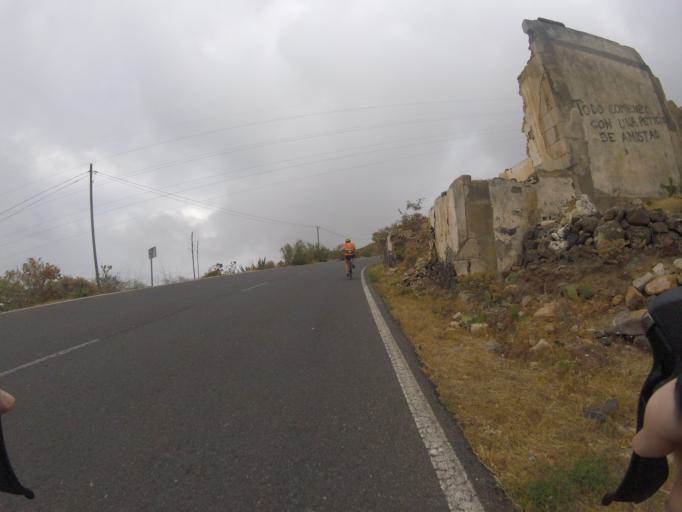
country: ES
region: Canary Islands
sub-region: Provincia de Santa Cruz de Tenerife
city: Guimar
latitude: 28.2918
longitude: -16.4027
